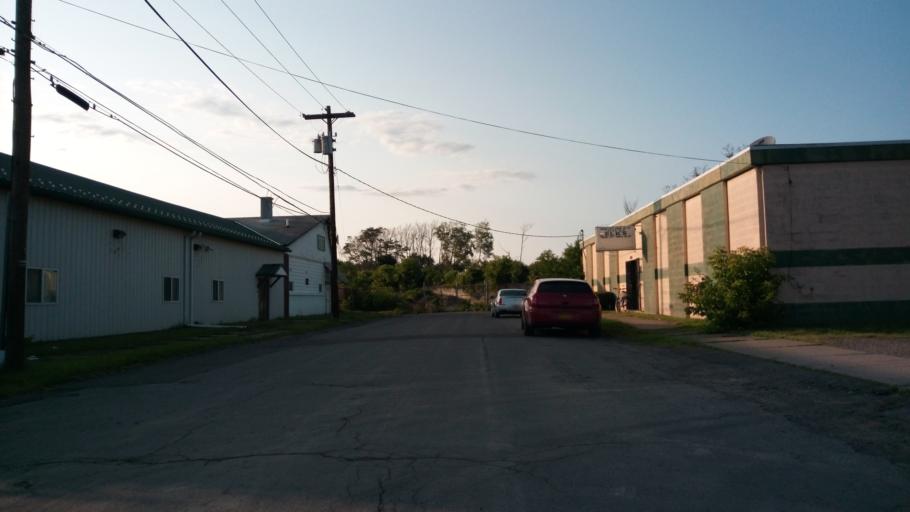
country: US
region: New York
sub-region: Chemung County
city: Elmira
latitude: 42.0992
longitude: -76.8056
